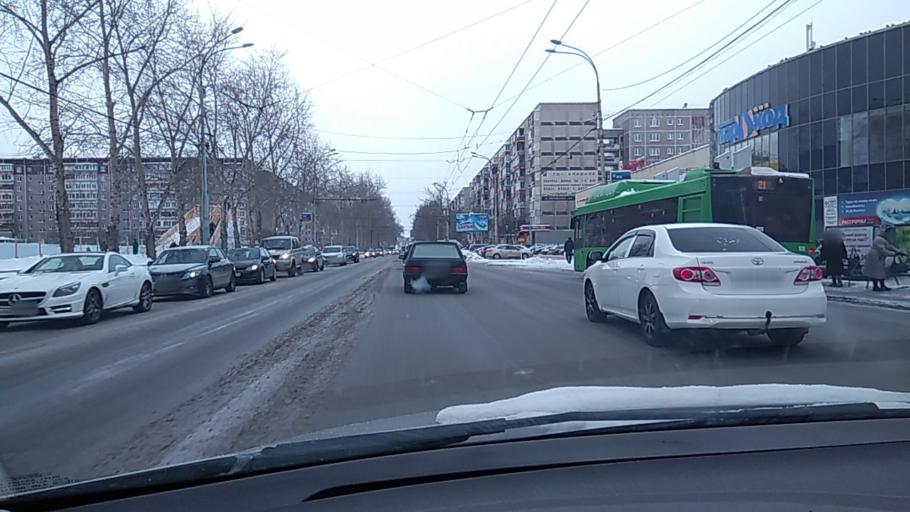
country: RU
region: Sverdlovsk
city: Sovkhoznyy
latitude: 56.7971
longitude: 60.5799
